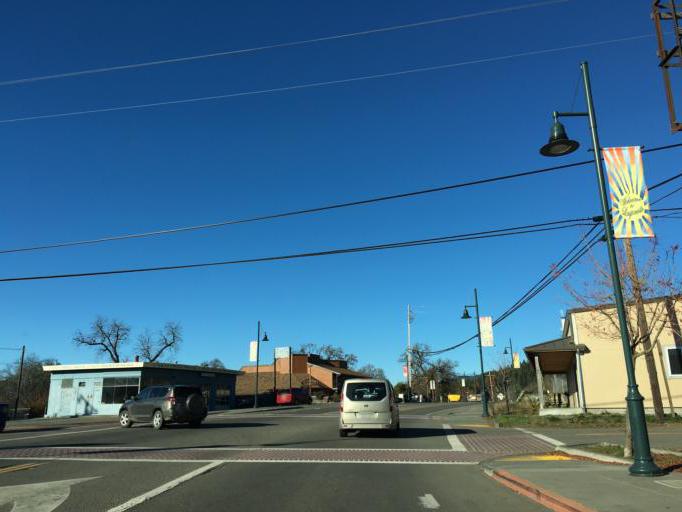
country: US
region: California
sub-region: Mendocino County
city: Laytonville
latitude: 39.6876
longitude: -123.4830
